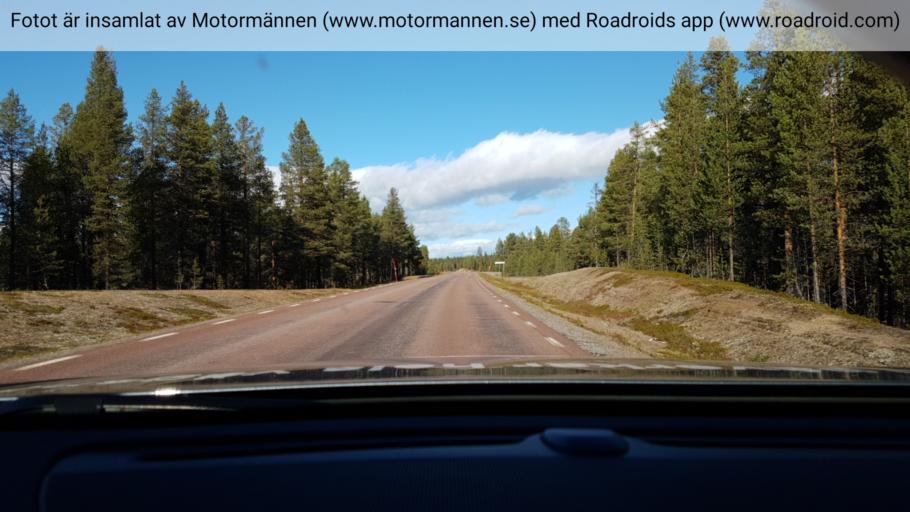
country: SE
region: Norrbotten
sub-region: Arjeplogs Kommun
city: Arjeplog
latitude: 66.0278
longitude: 18.0630
